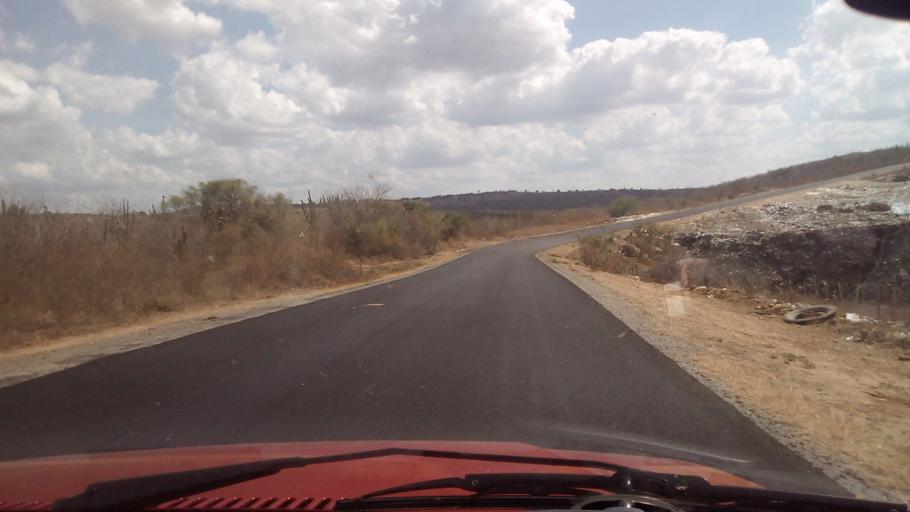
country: BR
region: Paraiba
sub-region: Bananeiras
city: Bananeiras
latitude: -6.7306
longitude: -35.7094
